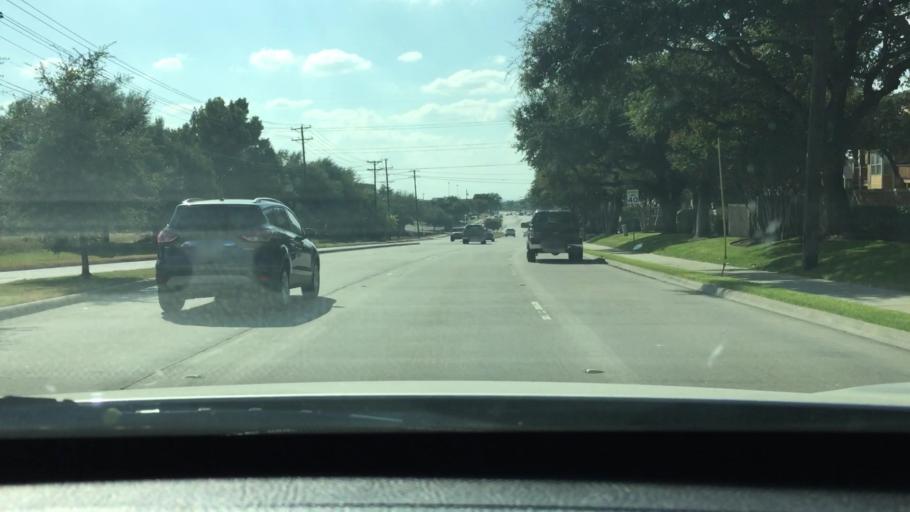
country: US
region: Texas
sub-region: Dallas County
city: Addison
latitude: 32.9871
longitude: -96.8484
